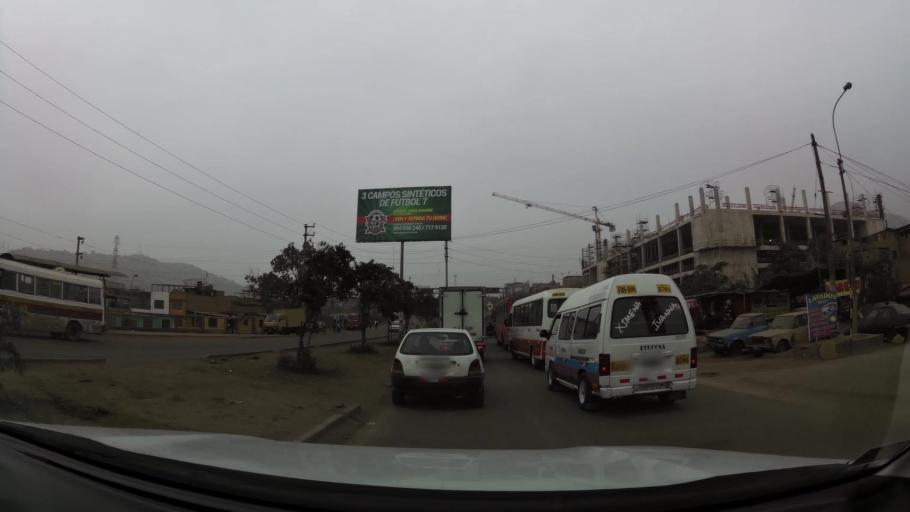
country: PE
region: Lima
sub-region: Lima
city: Surco
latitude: -12.1820
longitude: -76.9425
